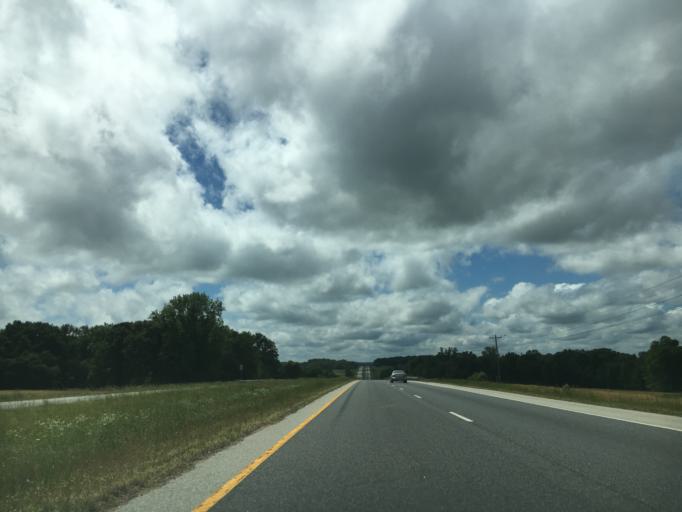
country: US
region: Virginia
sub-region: Mecklenburg County
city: Boydton
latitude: 36.6715
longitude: -78.2613
